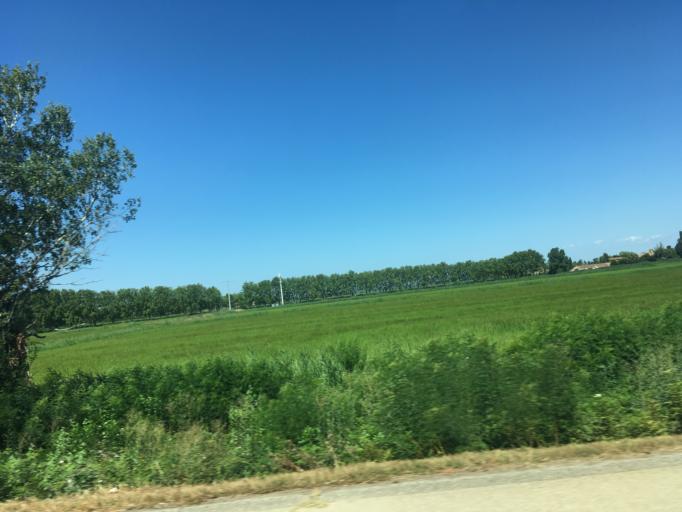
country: FR
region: Languedoc-Roussillon
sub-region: Departement du Gard
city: Saint-Gilles
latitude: 43.6128
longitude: 4.4794
